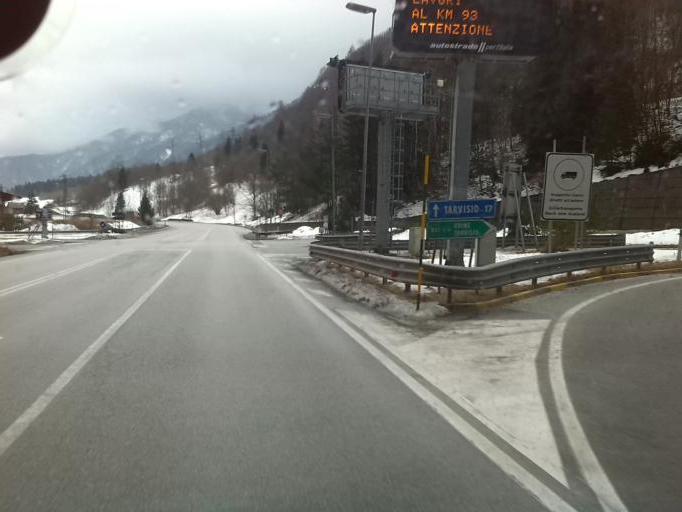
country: IT
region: Friuli Venezia Giulia
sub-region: Provincia di Udine
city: Pontebba
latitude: 46.5094
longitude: 13.3403
